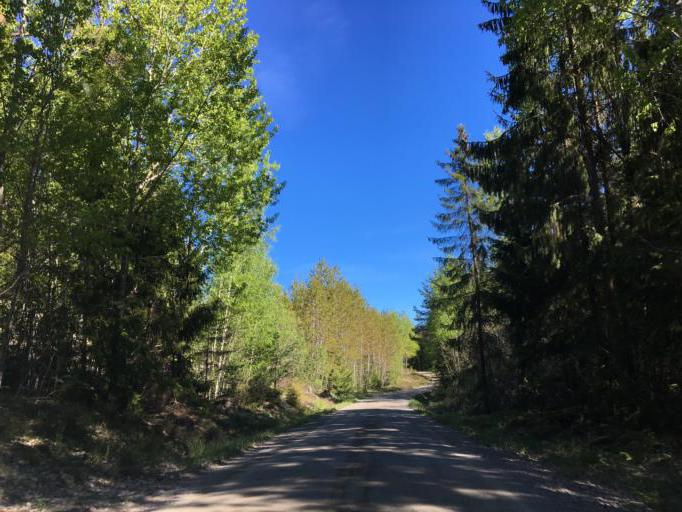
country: SE
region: Soedermanland
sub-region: Eskilstuna Kommun
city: Kvicksund
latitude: 59.3742
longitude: 16.2724
